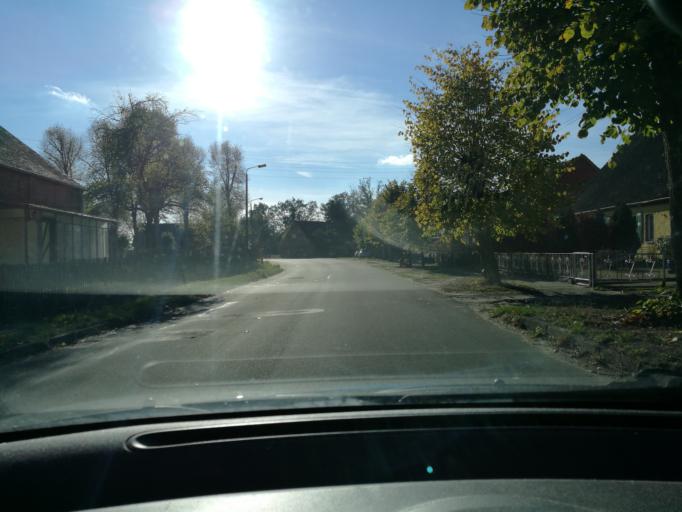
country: DE
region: Lower Saxony
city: Gorleben
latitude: 53.1208
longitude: 11.3569
